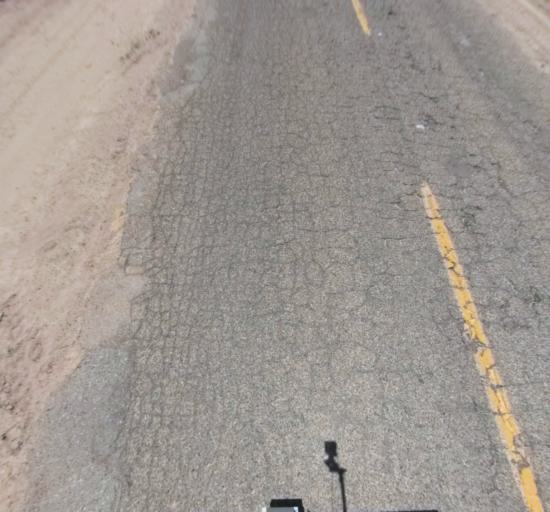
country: US
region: California
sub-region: Madera County
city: Madera Acres
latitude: 36.9964
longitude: -120.1444
